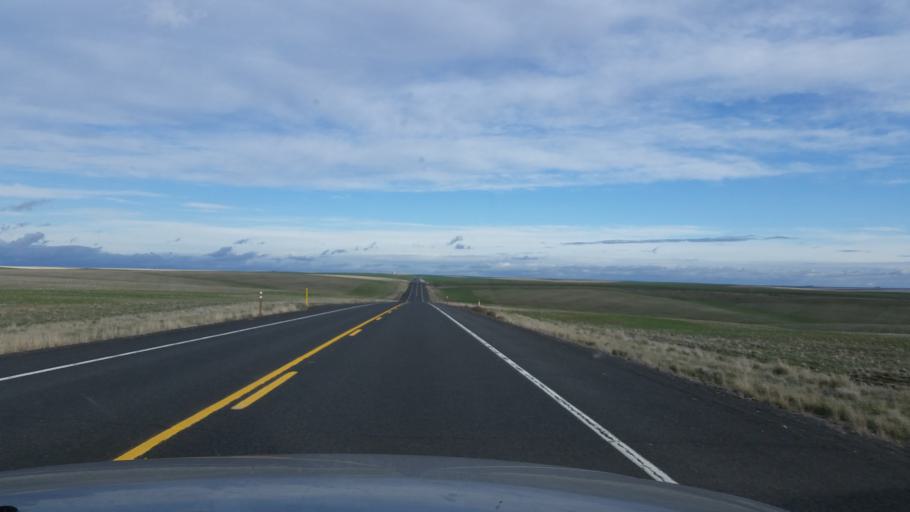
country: US
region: Washington
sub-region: Adams County
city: Ritzville
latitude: 47.3923
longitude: -118.4084
